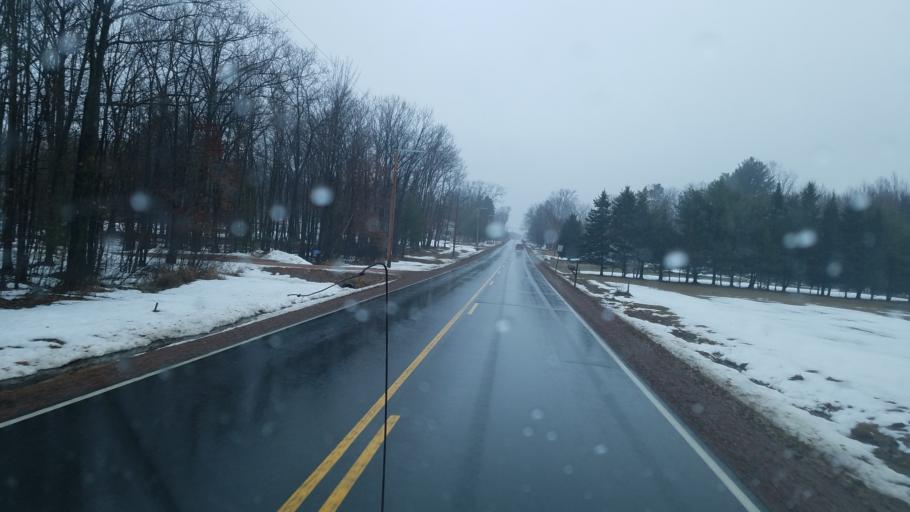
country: US
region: Wisconsin
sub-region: Wood County
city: Marshfield
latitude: 44.5502
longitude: -90.3000
